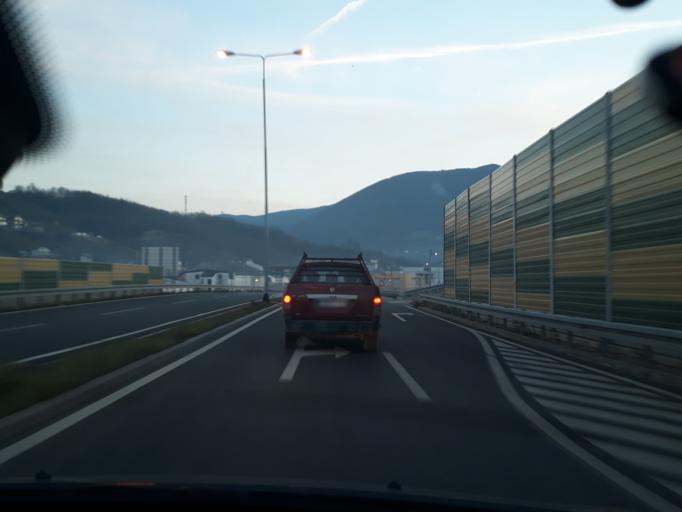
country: BA
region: Federation of Bosnia and Herzegovina
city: Hadzici
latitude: 43.8602
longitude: 18.2499
